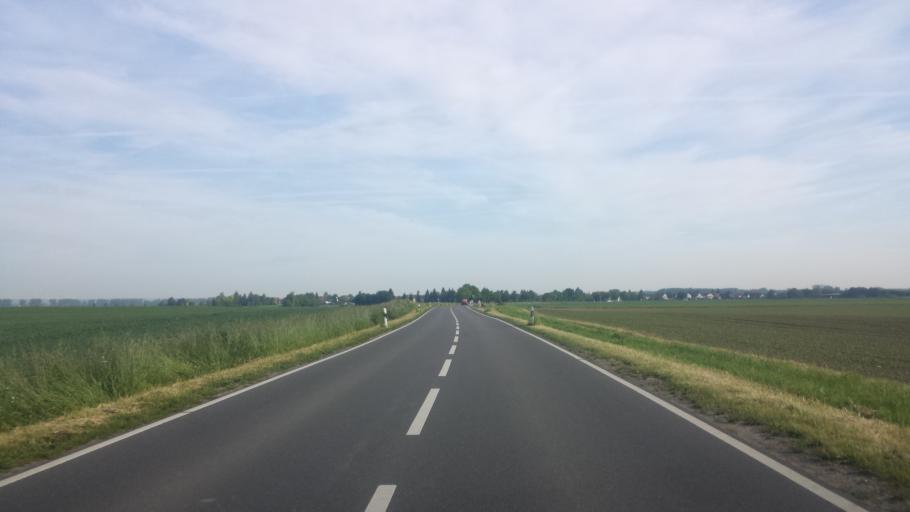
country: DE
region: Rheinland-Pfalz
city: Worms
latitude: 49.6699
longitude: 8.3890
